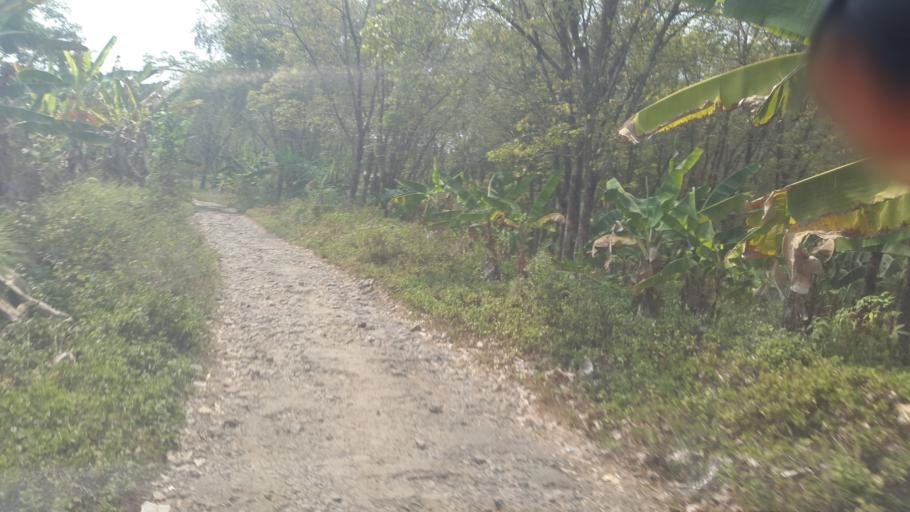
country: ID
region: West Java
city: Cimaja
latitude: -6.9334
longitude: 106.4984
